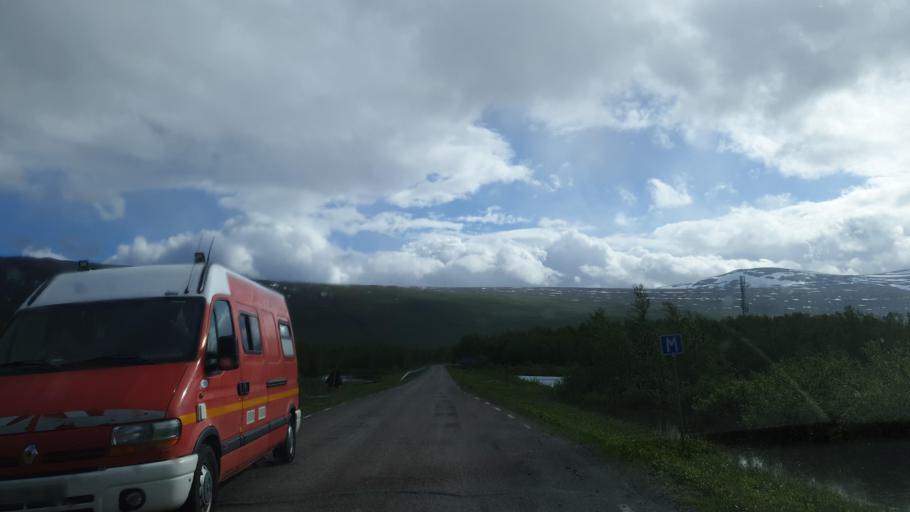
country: SE
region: Norrbotten
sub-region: Kiruna Kommun
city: Kiruna
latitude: 67.8532
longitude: 19.0190
